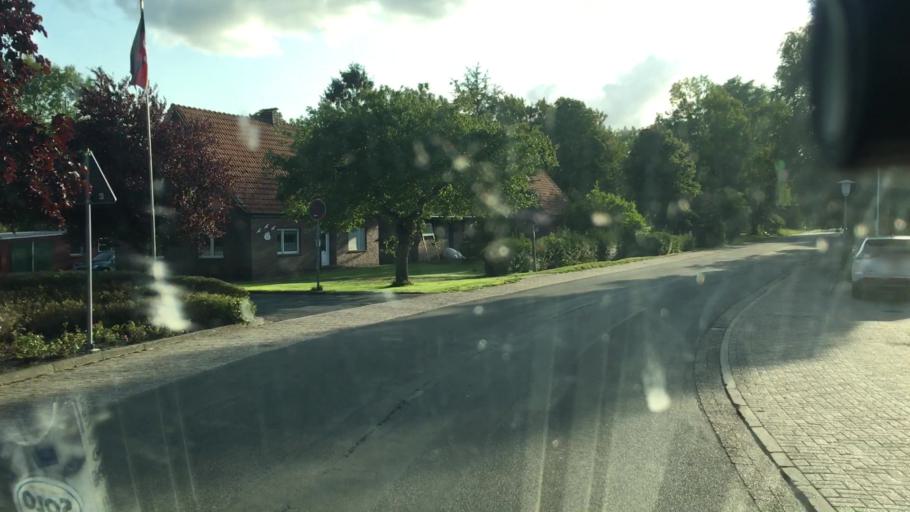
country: DE
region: Lower Saxony
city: Jever
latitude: 53.6343
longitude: 7.8416
